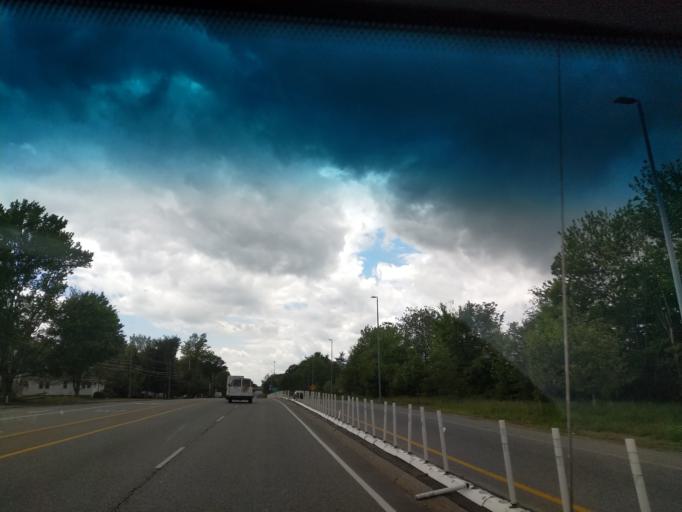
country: US
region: Maine
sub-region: Cumberland County
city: South Portland Gardens
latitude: 43.6302
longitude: -70.3121
